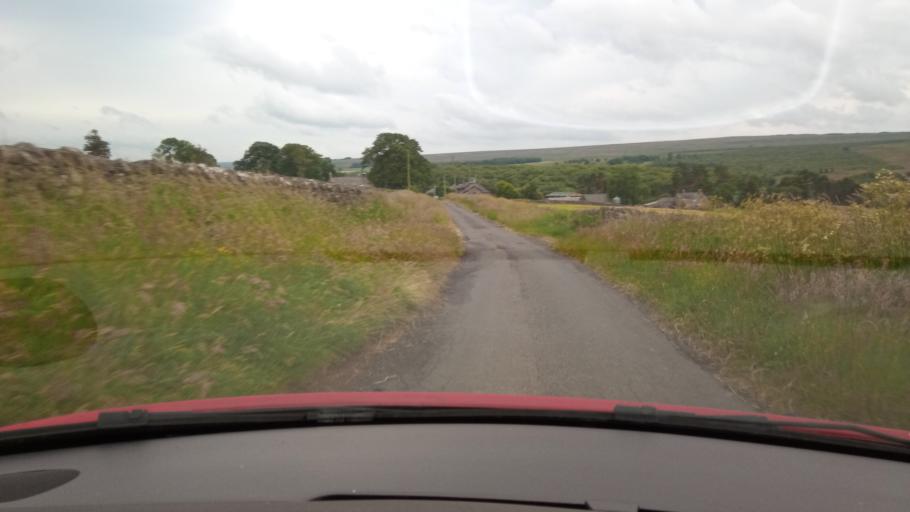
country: GB
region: England
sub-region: Northumberland
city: Rochester
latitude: 55.2796
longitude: -2.2651
